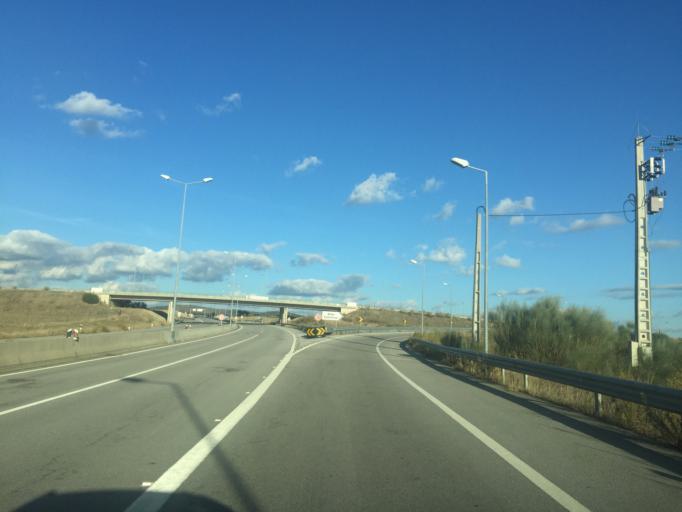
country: PT
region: Portalegre
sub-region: Alter do Chao
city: Alter do Chao
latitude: 39.1971
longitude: -7.6987
